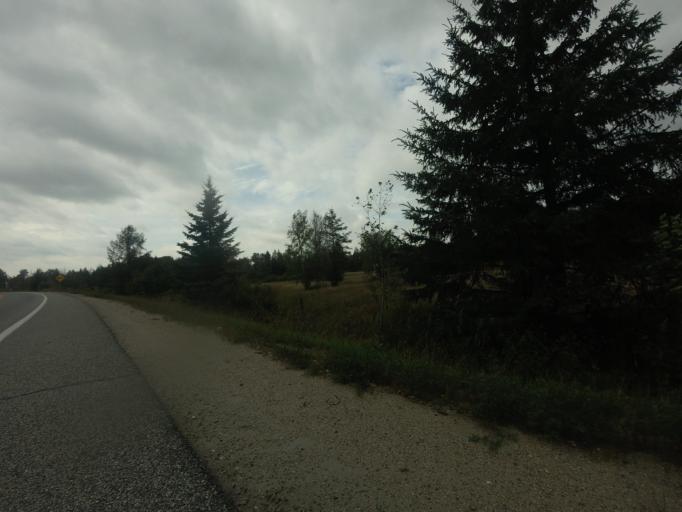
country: CA
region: Quebec
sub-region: Outaouais
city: Wakefield
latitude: 45.9047
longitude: -76.0258
